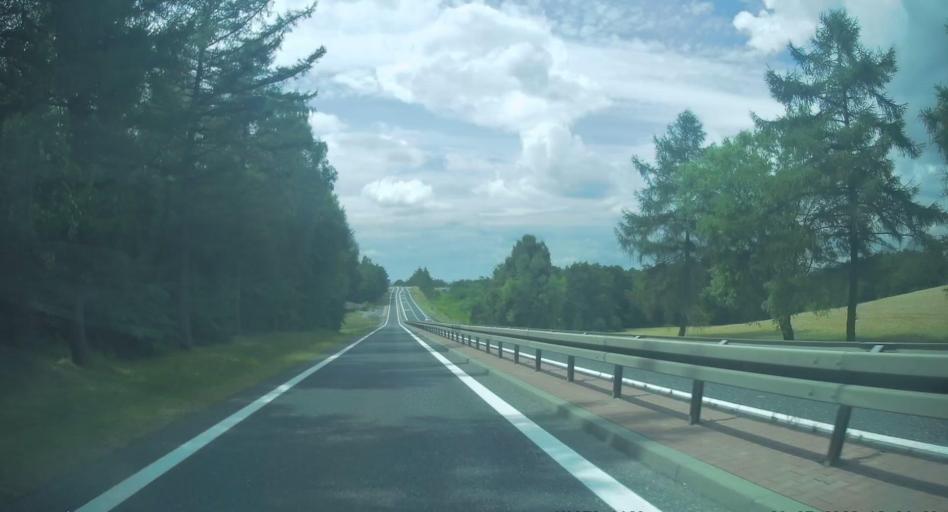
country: PL
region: Subcarpathian Voivodeship
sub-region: Powiat ropczycko-sedziszowski
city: Ropczyce
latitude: 50.0611
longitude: 21.5769
